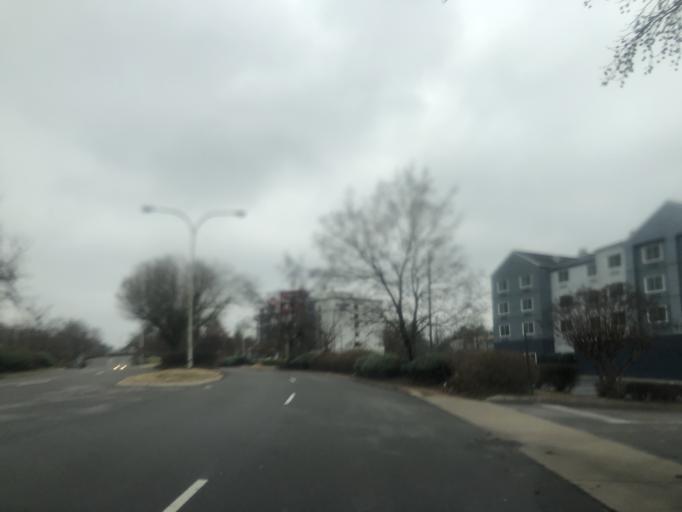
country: US
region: Tennessee
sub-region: Davidson County
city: Lakewood
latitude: 36.1466
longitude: -86.6627
